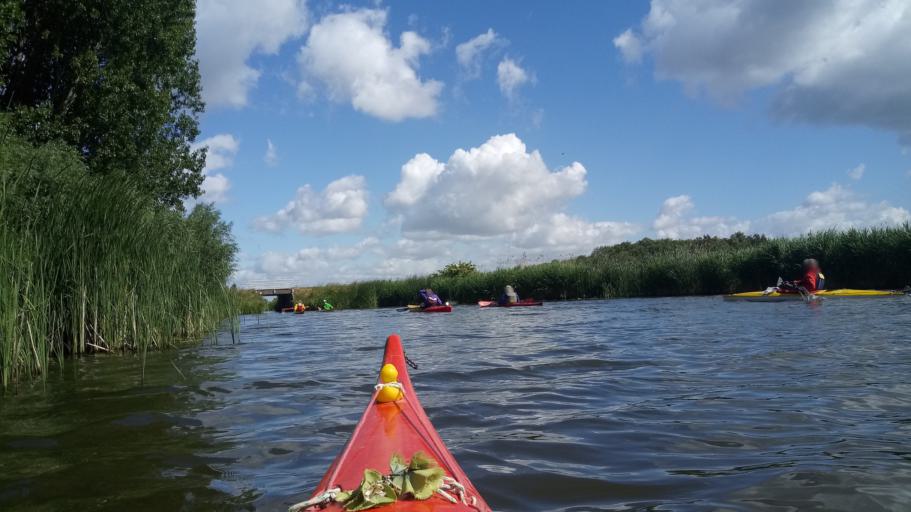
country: NL
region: North Holland
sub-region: Gemeente Enkhuizen
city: Enkhuizen
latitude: 52.7057
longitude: 5.1976
